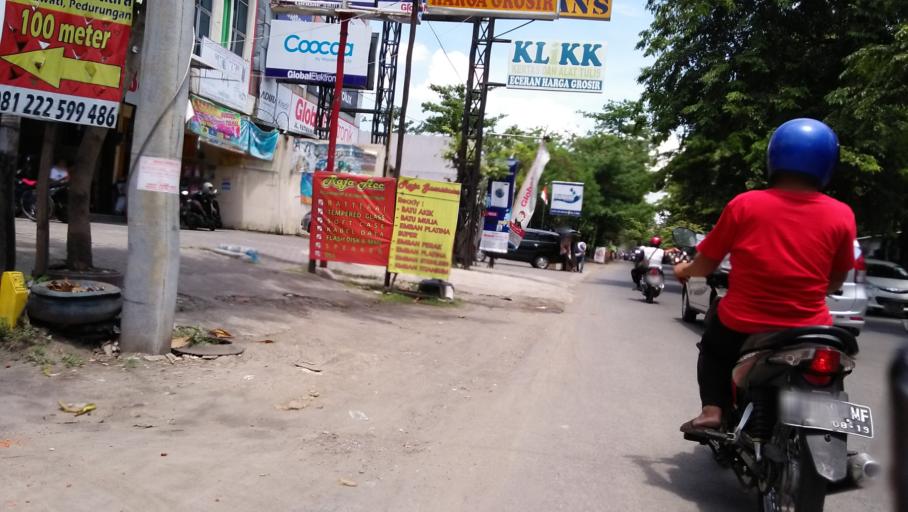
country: ID
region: Central Java
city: Mranggen
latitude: -7.0187
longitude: 110.4711
